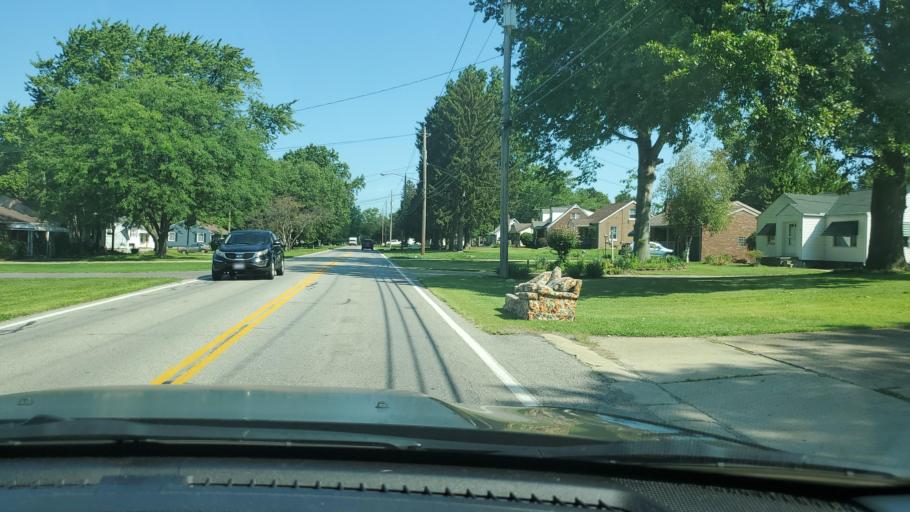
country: US
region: Ohio
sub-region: Trumbull County
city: Girard
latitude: 41.1644
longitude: -80.6894
